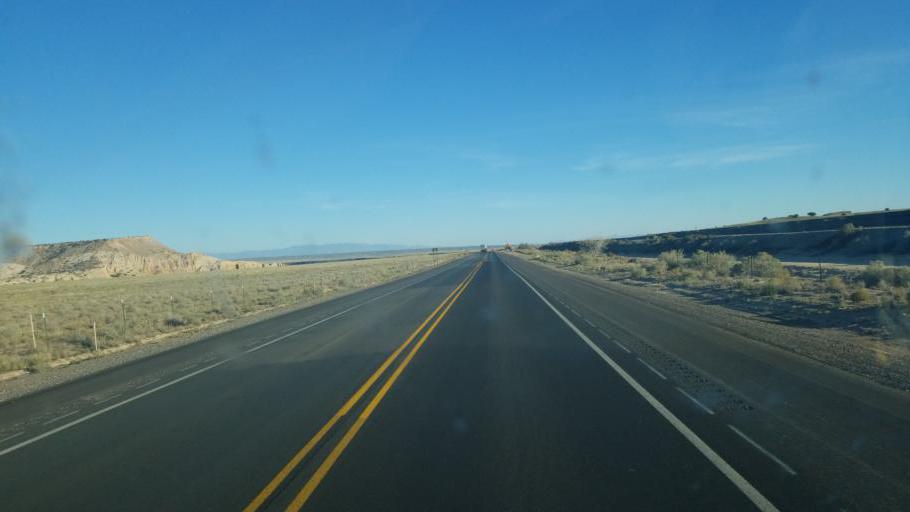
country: US
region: New Mexico
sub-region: Cibola County
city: Laguna
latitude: 34.9079
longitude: -107.0947
